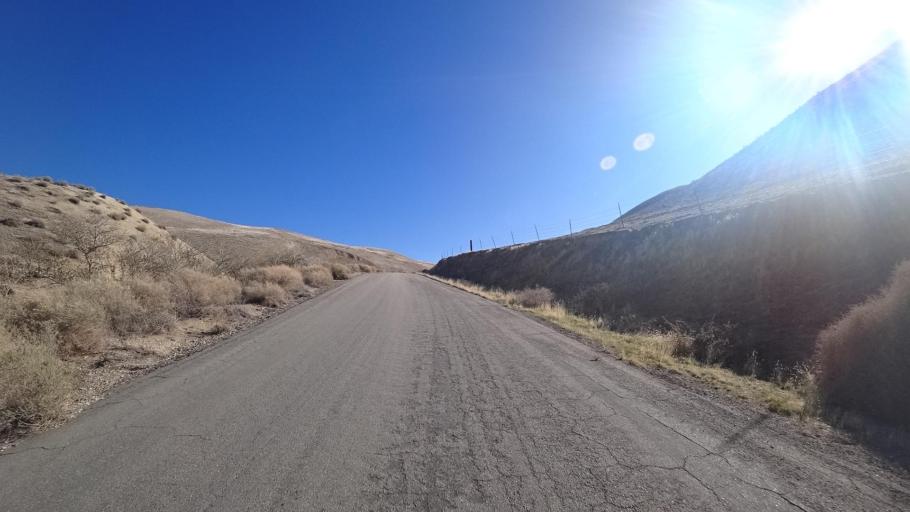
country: US
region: California
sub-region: Kern County
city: Maricopa
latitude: 34.9628
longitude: -119.4125
